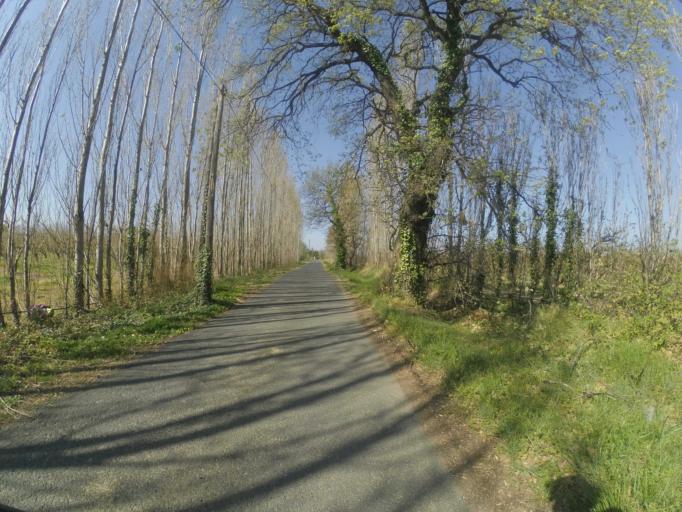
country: FR
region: Languedoc-Roussillon
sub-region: Departement des Pyrenees-Orientales
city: Thuir
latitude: 42.6541
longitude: 2.7619
